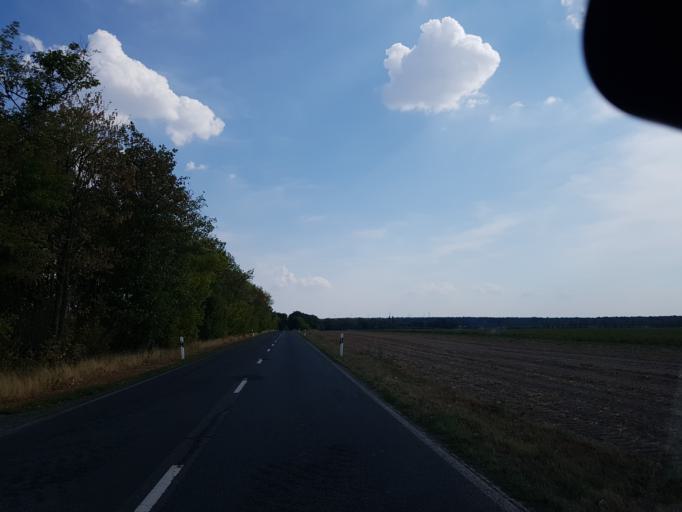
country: DE
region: Saxony-Anhalt
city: Zahna
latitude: 51.9788
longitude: 12.8601
